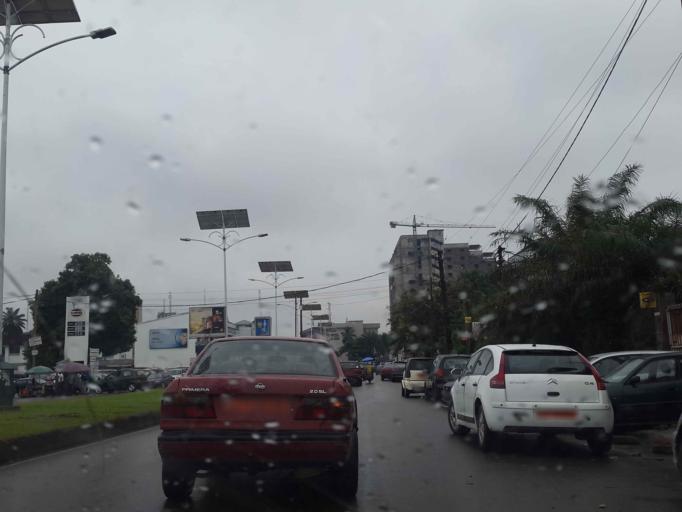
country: CM
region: Littoral
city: Douala
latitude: 4.0585
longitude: 9.7011
